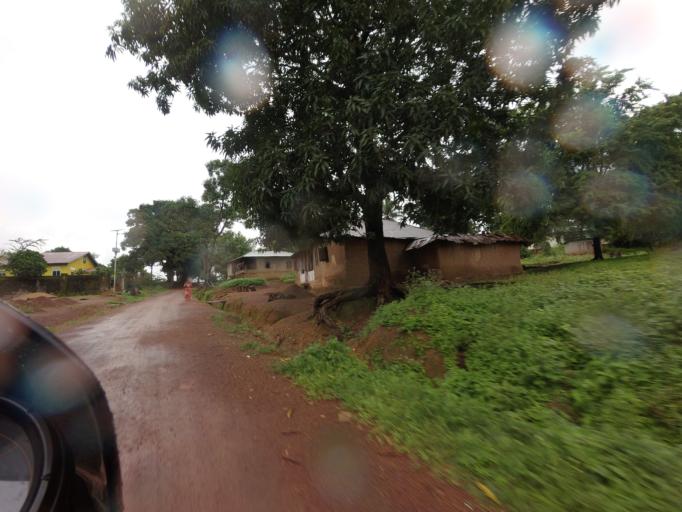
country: SL
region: Northern Province
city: Kambia
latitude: 9.1209
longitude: -12.9203
